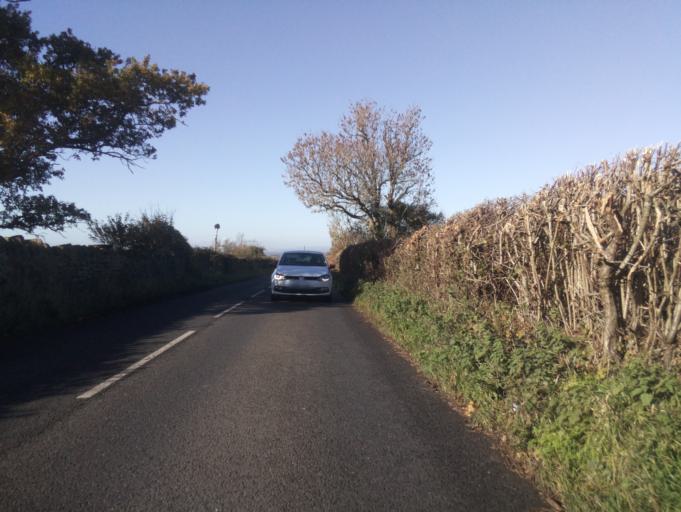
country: GB
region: England
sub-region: Somerset
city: Yeovil
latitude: 50.9616
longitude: -2.6690
